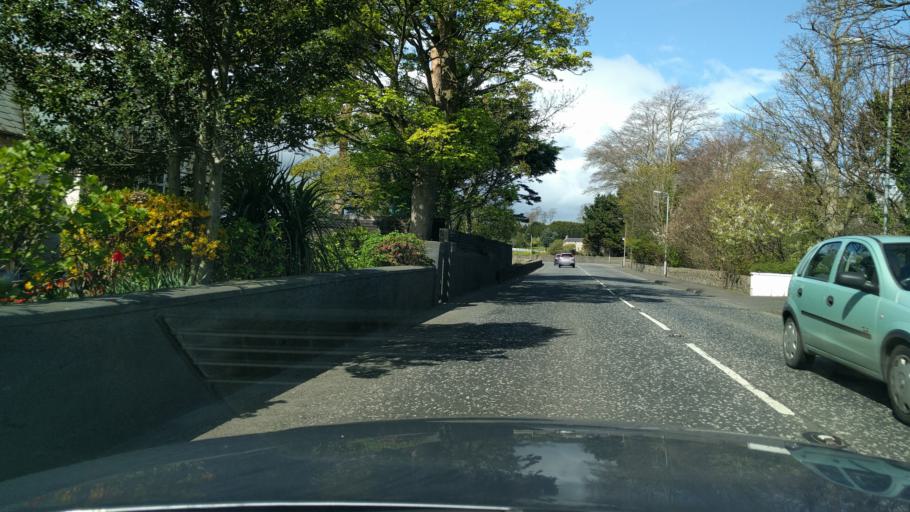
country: GB
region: Northern Ireland
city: Rostrevor
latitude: 54.0996
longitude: -6.2129
